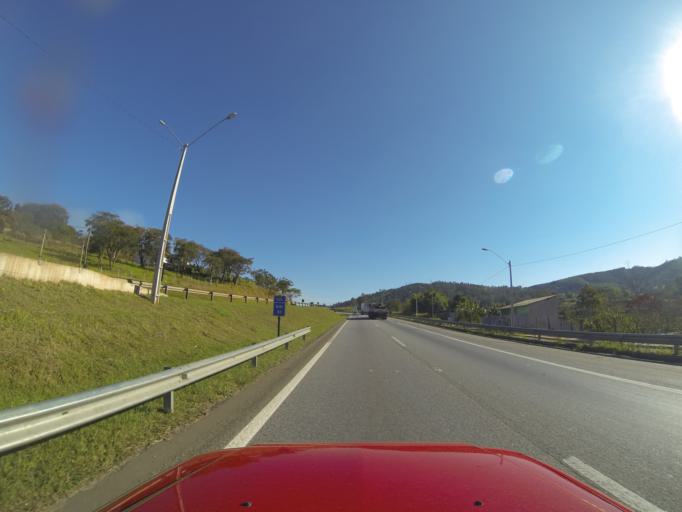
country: BR
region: Sao Paulo
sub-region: Atibaia
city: Atibaia
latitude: -23.0548
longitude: -46.5697
